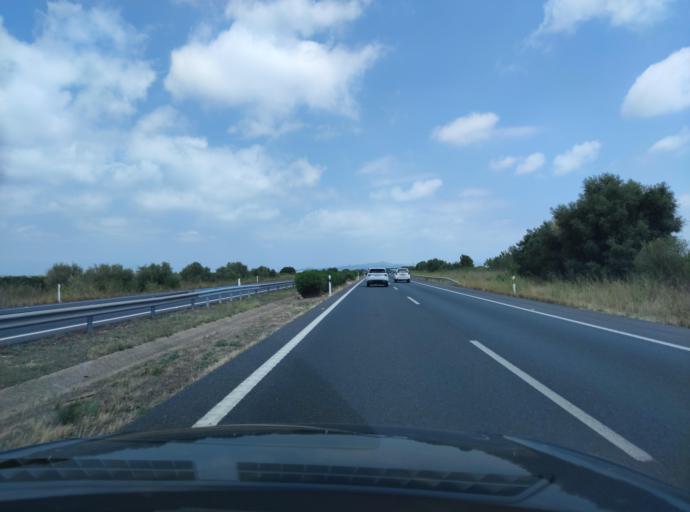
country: ES
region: Catalonia
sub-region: Provincia de Tarragona
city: Alcanar
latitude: 40.5171
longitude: 0.4157
